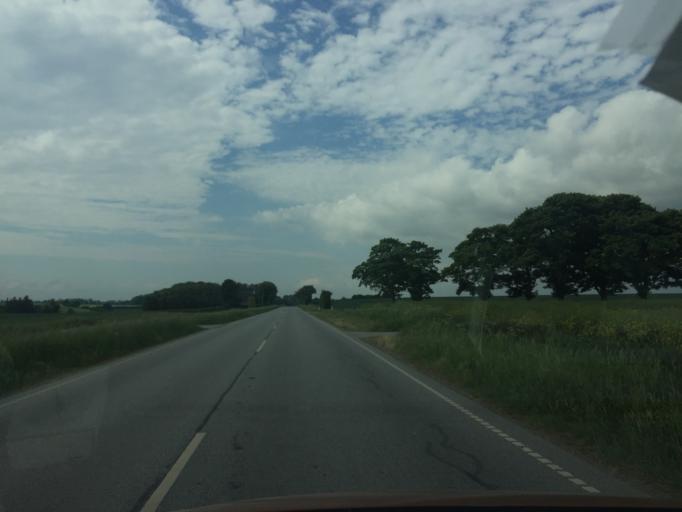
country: DK
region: South Denmark
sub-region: Haderslev Kommune
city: Starup
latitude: 55.2528
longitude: 9.5991
